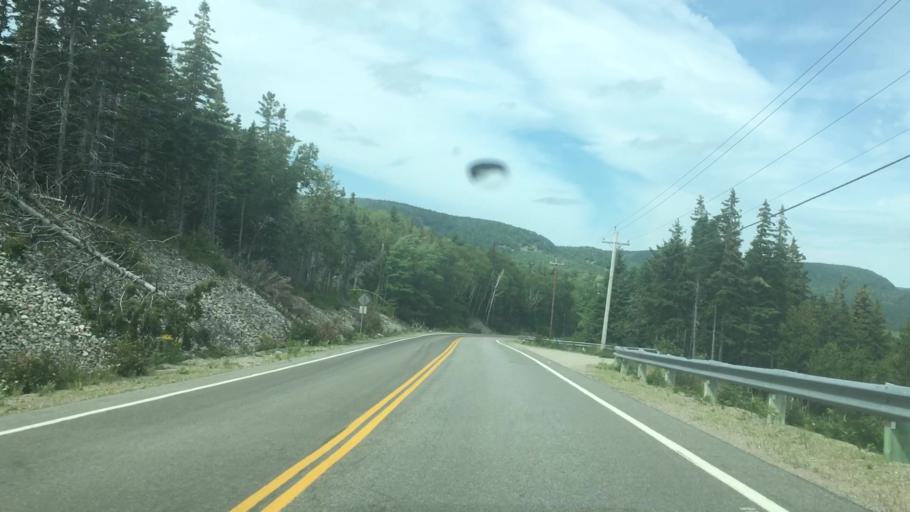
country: CA
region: Nova Scotia
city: Sydney Mines
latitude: 46.5378
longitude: -60.4136
